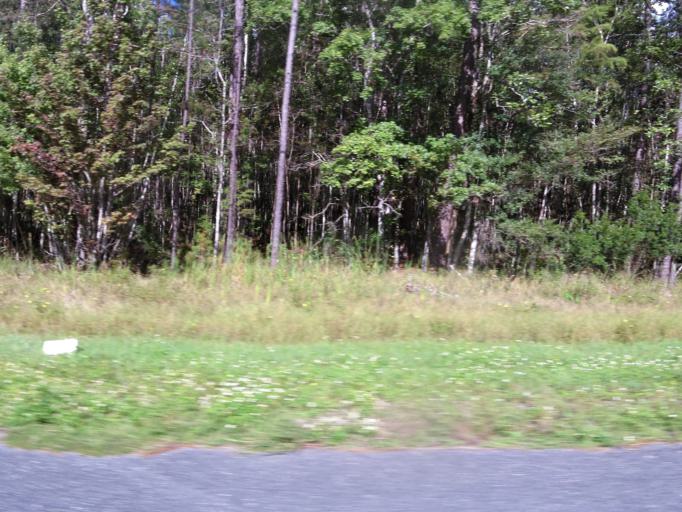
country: US
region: Florida
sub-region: Saint Johns County
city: Fruit Cove
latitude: 30.0542
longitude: -81.6077
